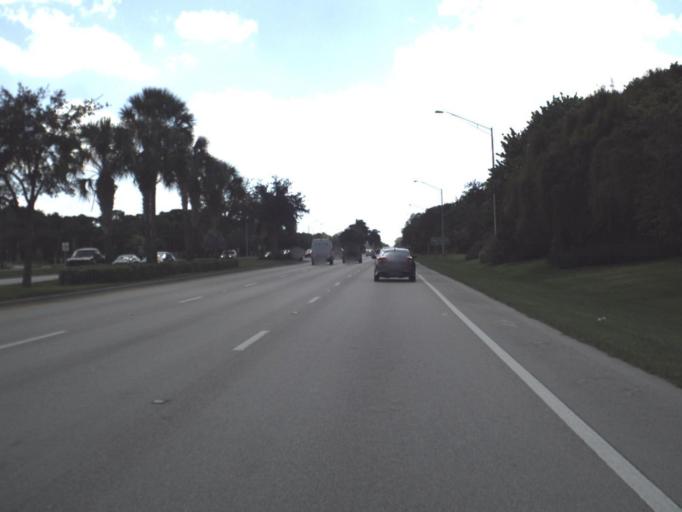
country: US
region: Florida
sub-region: Collier County
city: Pelican Bay
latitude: 26.2370
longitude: -81.8010
